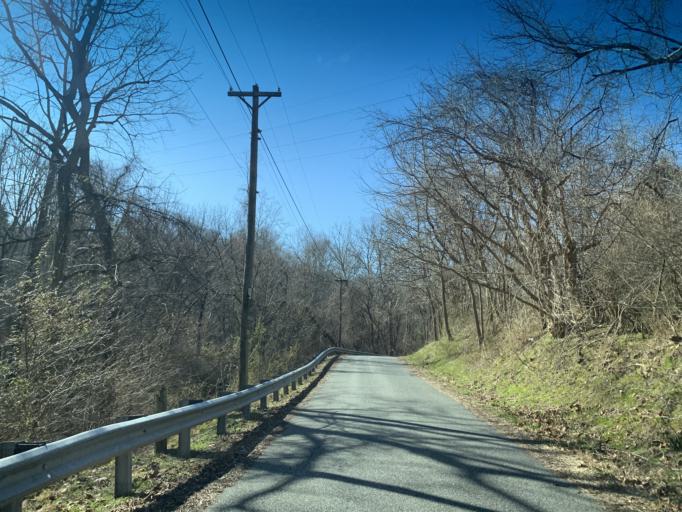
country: US
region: Maryland
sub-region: Cecil County
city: Rising Sun
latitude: 39.6881
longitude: -76.1249
